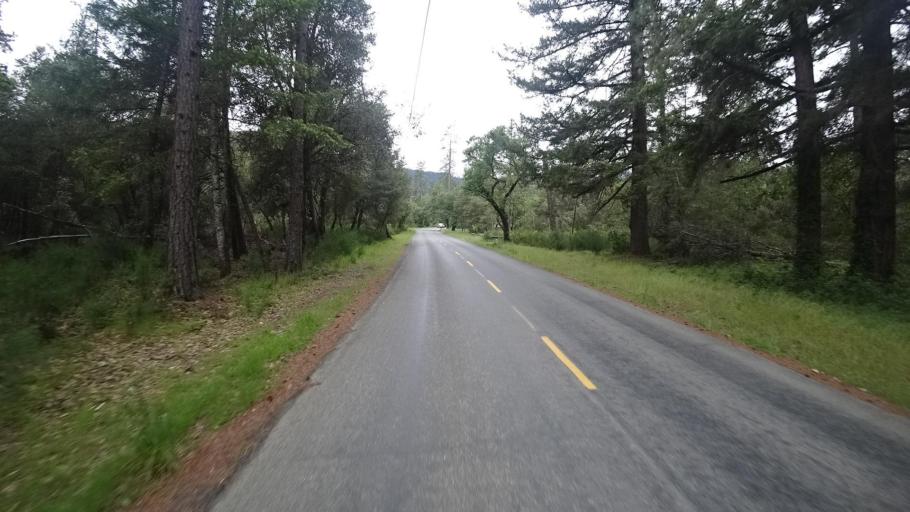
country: US
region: California
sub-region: Humboldt County
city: Willow Creek
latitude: 40.9475
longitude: -123.6267
